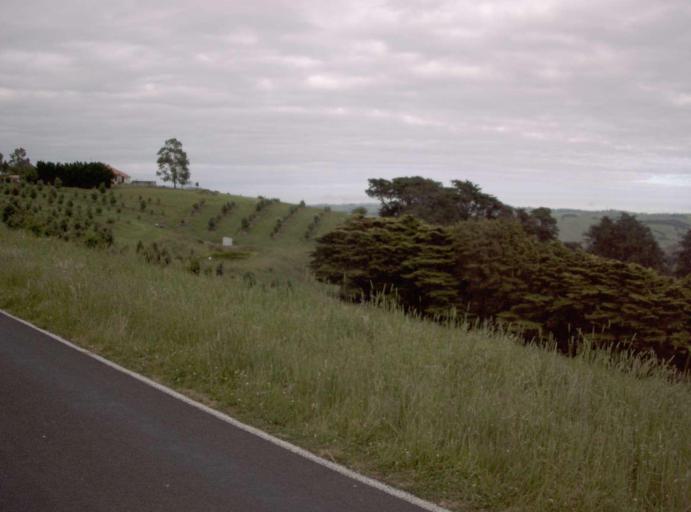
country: AU
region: Victoria
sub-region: Bass Coast
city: North Wonthaggi
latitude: -38.4797
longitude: 145.7590
